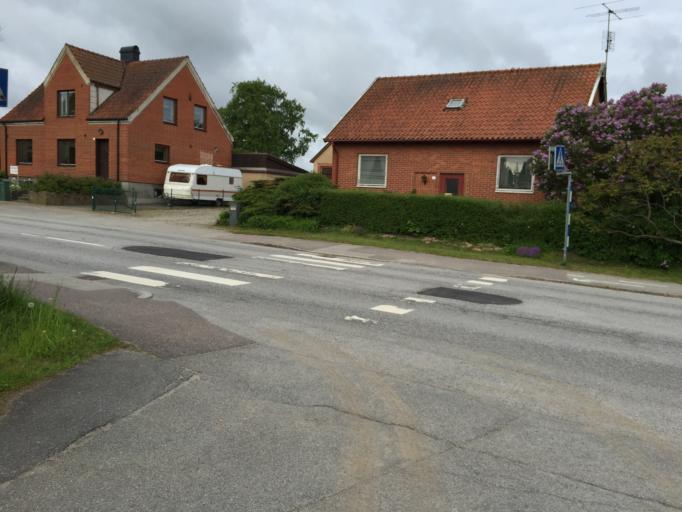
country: SE
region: Skane
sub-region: Lunds Kommun
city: Veberod
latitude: 55.6328
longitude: 13.4921
